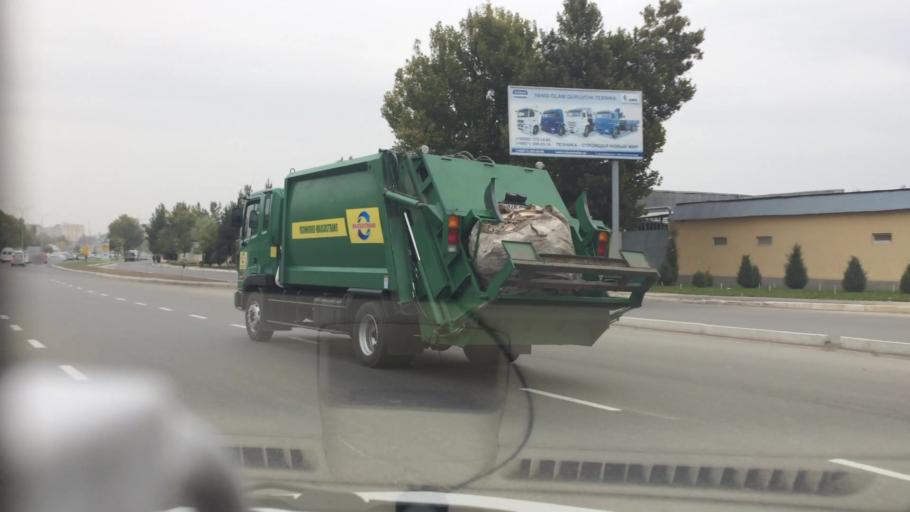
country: UZ
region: Toshkent
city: Salor
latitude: 41.3001
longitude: 69.3465
